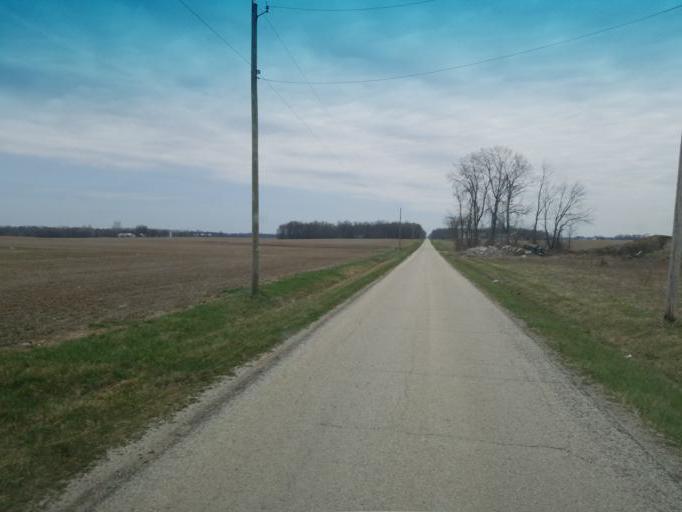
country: US
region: Ohio
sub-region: Crawford County
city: Bucyrus
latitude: 40.8920
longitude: -82.9991
